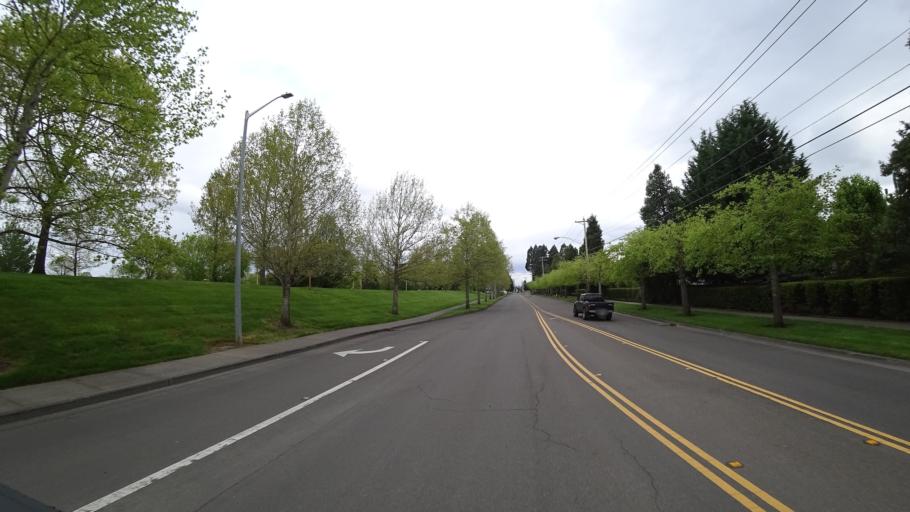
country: US
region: Oregon
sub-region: Washington County
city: Hillsboro
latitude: 45.5419
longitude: -122.9664
